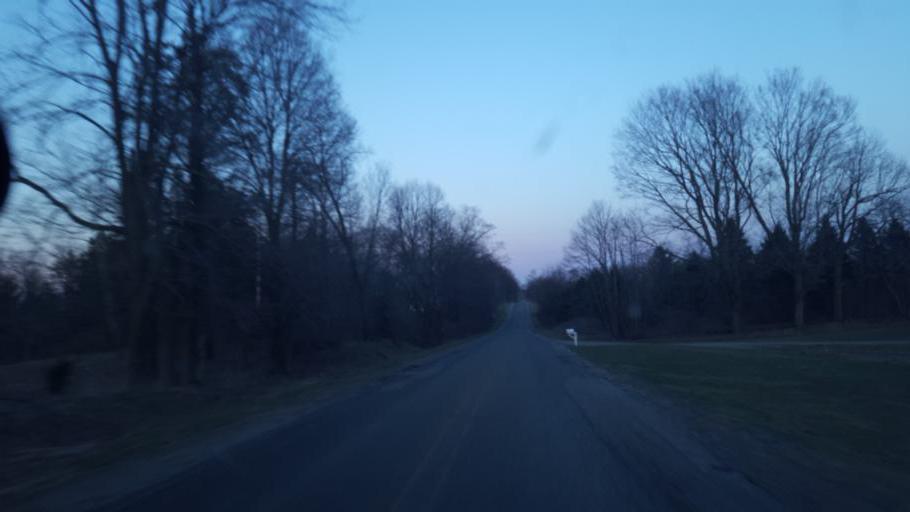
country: US
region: Michigan
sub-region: Montcalm County
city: Howard City
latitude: 43.5261
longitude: -85.4641
